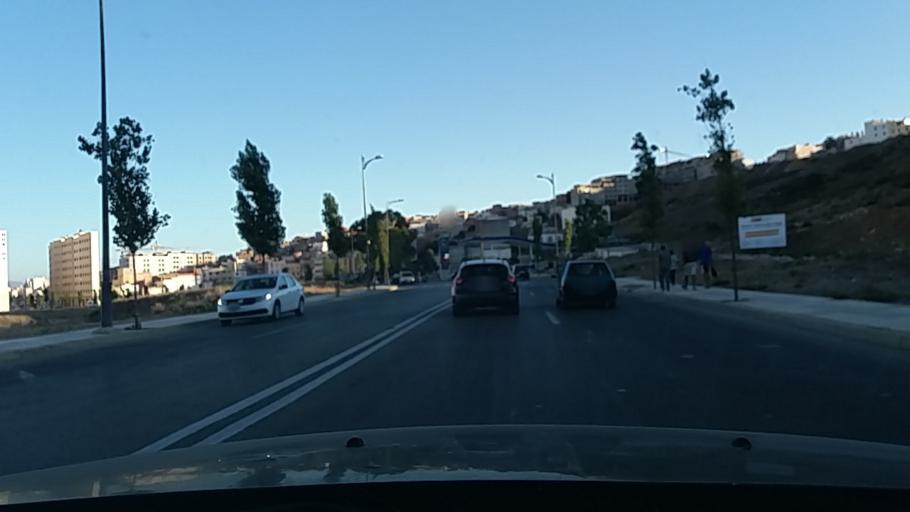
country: MA
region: Tanger-Tetouan
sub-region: Tanger-Assilah
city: Boukhalef
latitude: 35.7694
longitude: -5.8591
